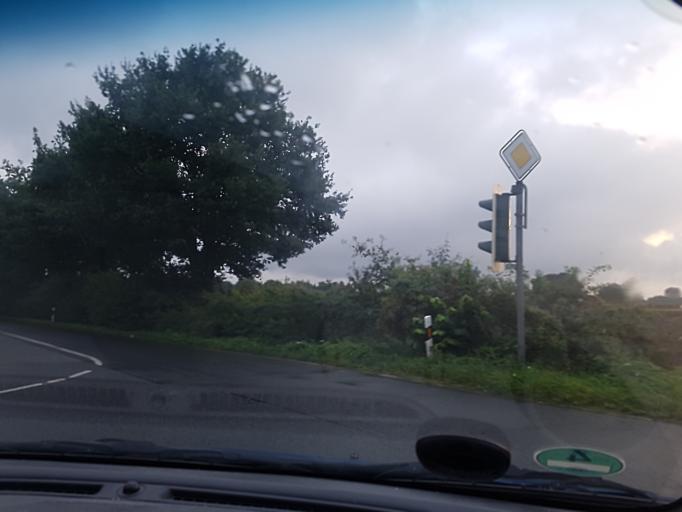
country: DE
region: Lower Saxony
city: Garbsen-Mitte
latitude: 52.4389
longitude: 9.6437
